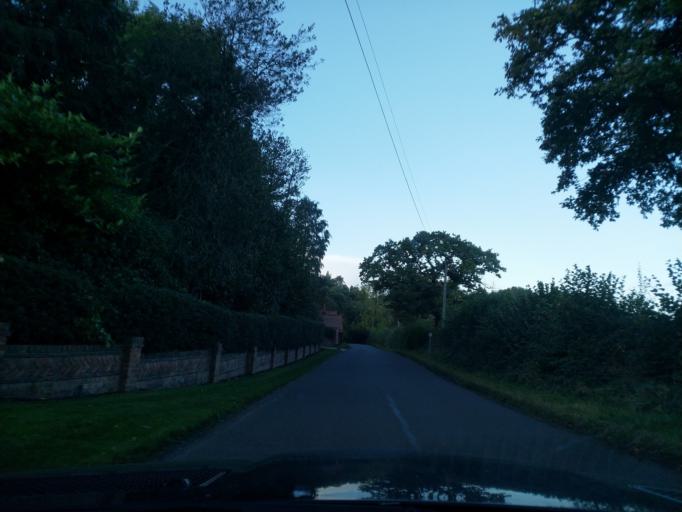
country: GB
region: England
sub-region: Solihull
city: Knowle
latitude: 52.3414
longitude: -1.7458
